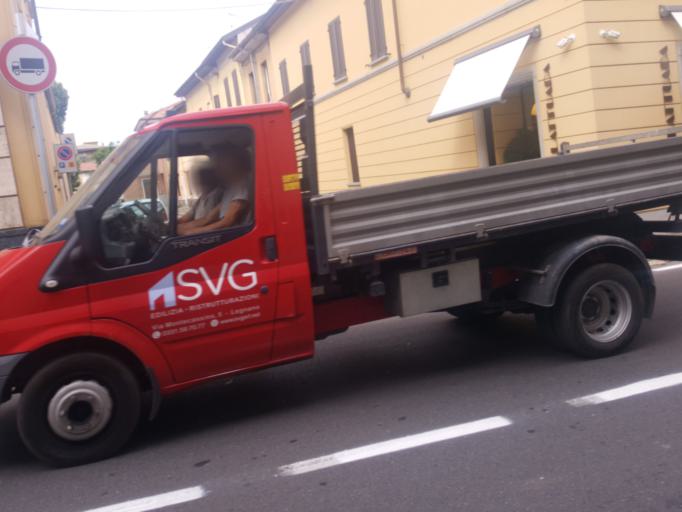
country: IT
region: Lombardy
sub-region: Citta metropolitana di Milano
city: San Vittore Olona
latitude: 45.5867
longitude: 8.9420
